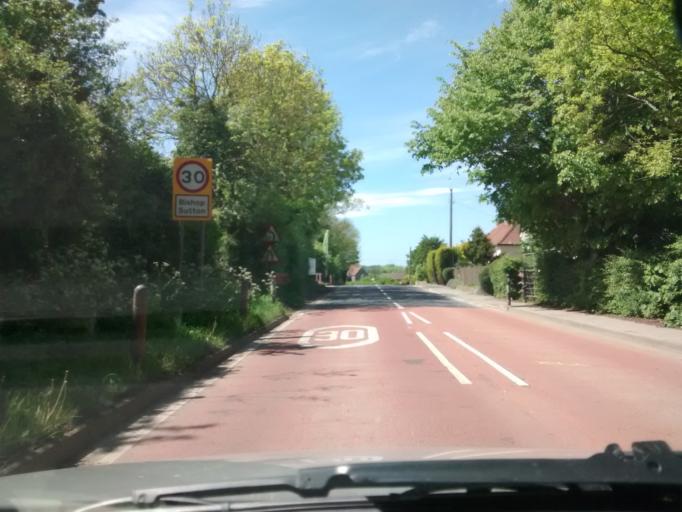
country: GB
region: England
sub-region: Bath and North East Somerset
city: Stanton Drew
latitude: 51.3365
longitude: -2.5911
